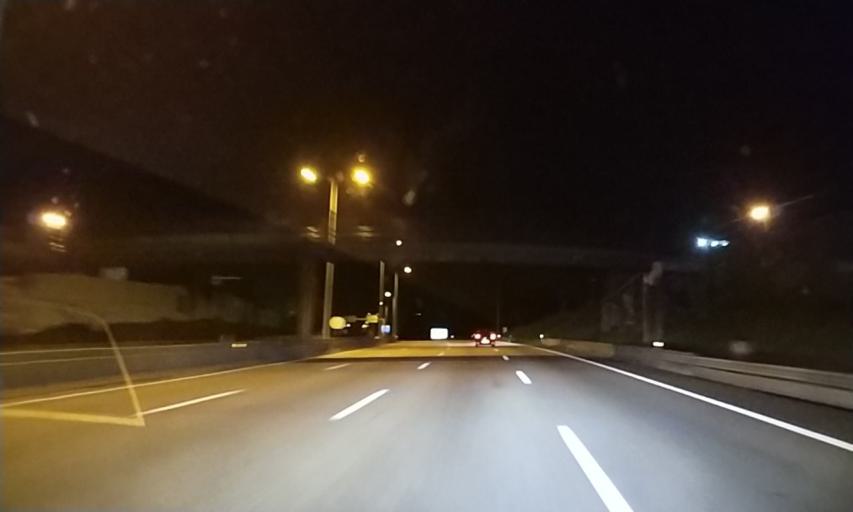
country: PT
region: Porto
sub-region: Maia
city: Pedroucos
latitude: 41.1750
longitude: -8.5938
